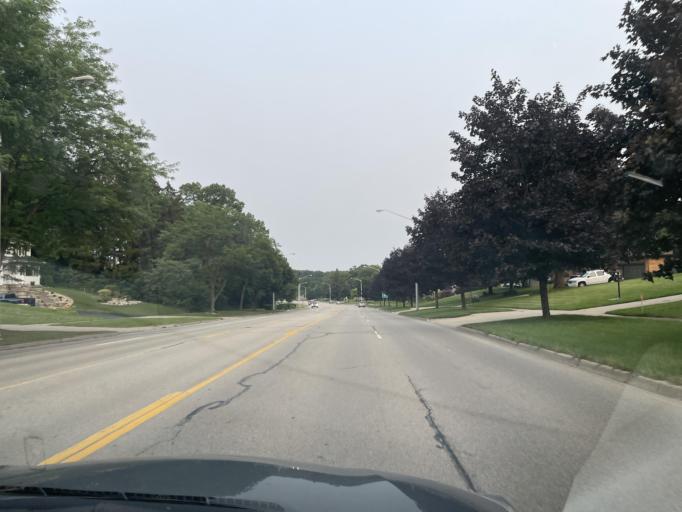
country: US
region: Michigan
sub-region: Kent County
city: Grand Rapids
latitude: 42.9686
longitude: -85.7131
